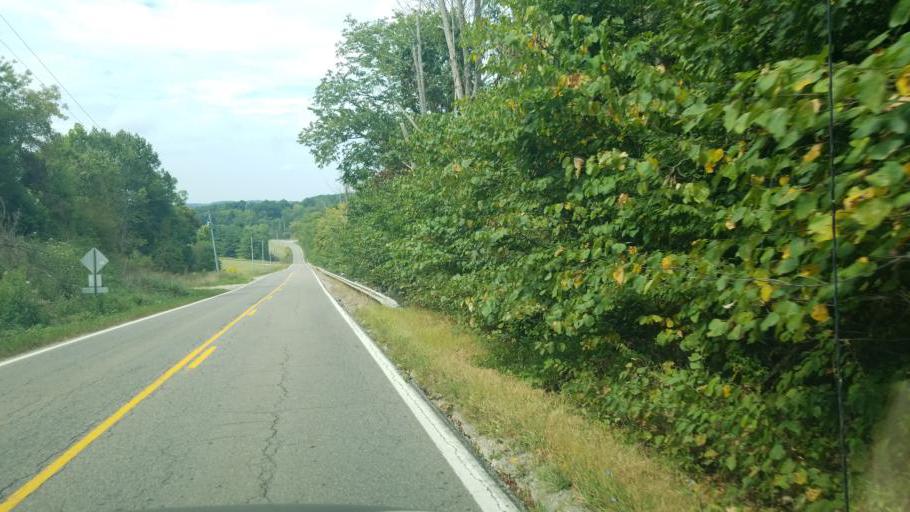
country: US
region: Ohio
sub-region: Licking County
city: Newark
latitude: 39.9936
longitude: -82.2645
